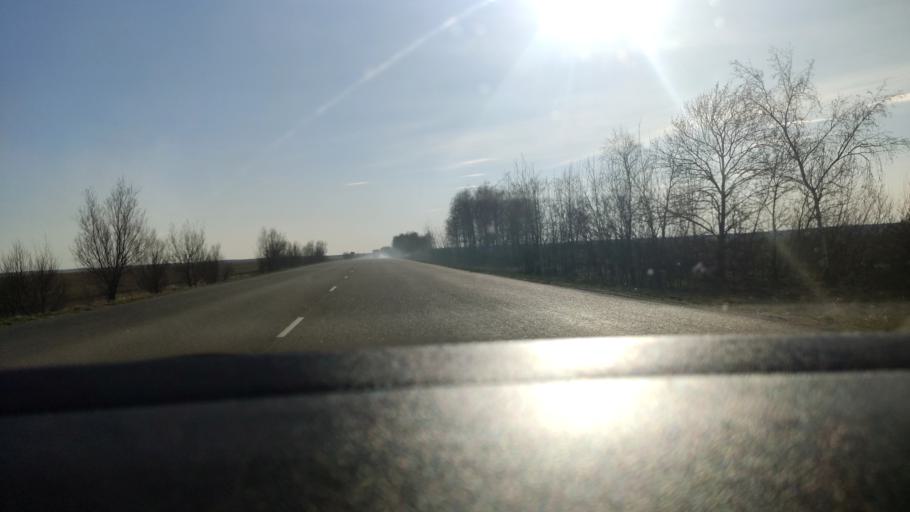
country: RU
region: Voronezj
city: Kolodeznyy
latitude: 51.3262
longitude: 39.1262
